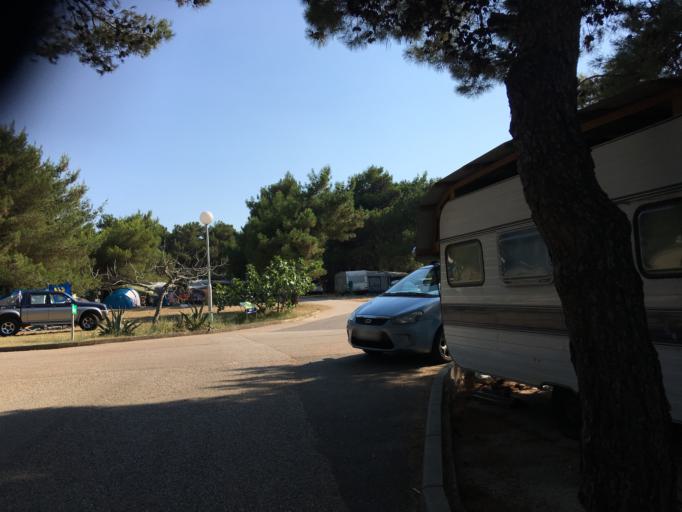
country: HR
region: Primorsko-Goranska
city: Punat
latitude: 45.0150
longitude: 14.6284
